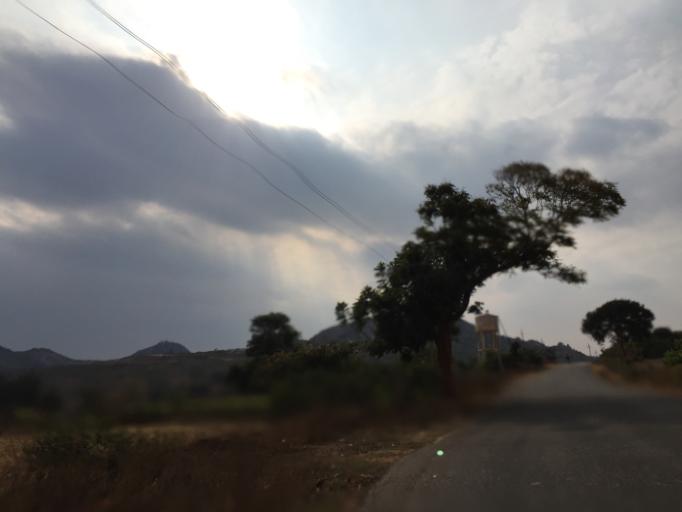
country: IN
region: Karnataka
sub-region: Chikkaballapur
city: Chik Ballapur
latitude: 13.5522
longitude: 77.7501
